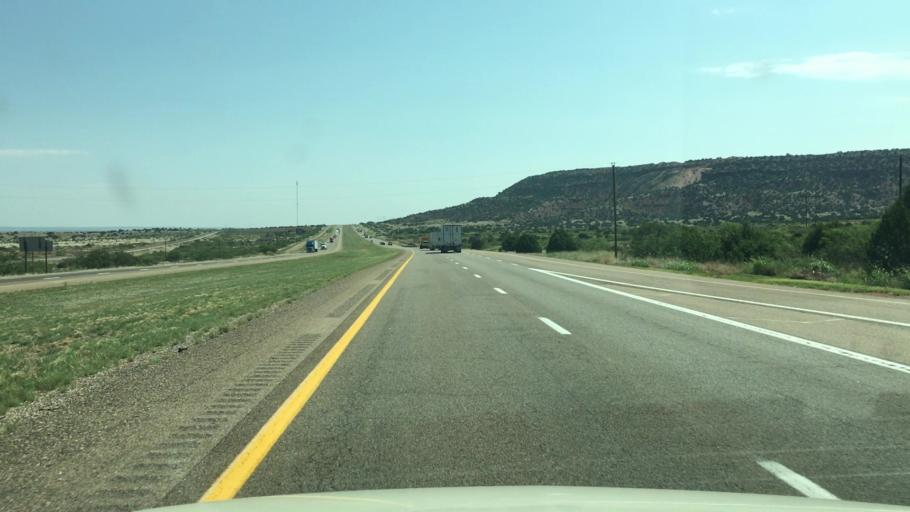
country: US
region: New Mexico
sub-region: Guadalupe County
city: Santa Rosa
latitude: 35.0352
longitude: -104.4001
